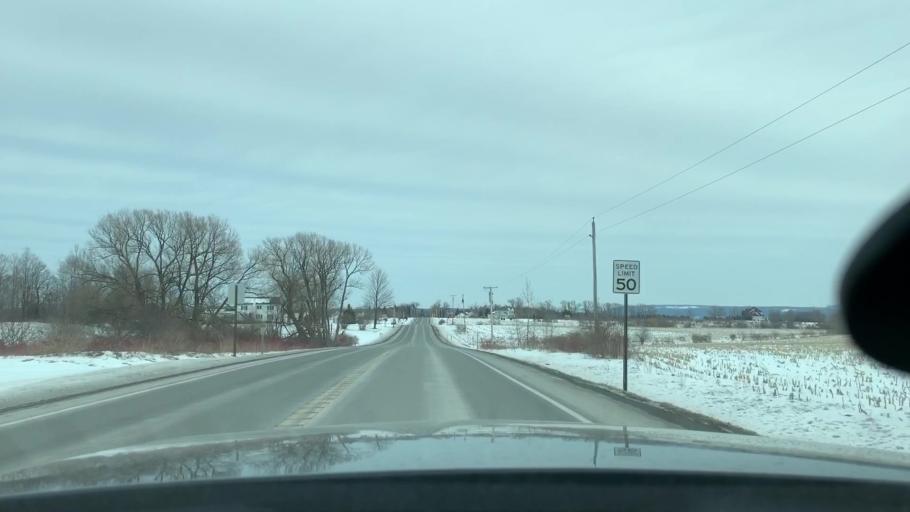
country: US
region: New York
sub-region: Herkimer County
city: Frankfort
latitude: 43.0332
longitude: -75.1184
